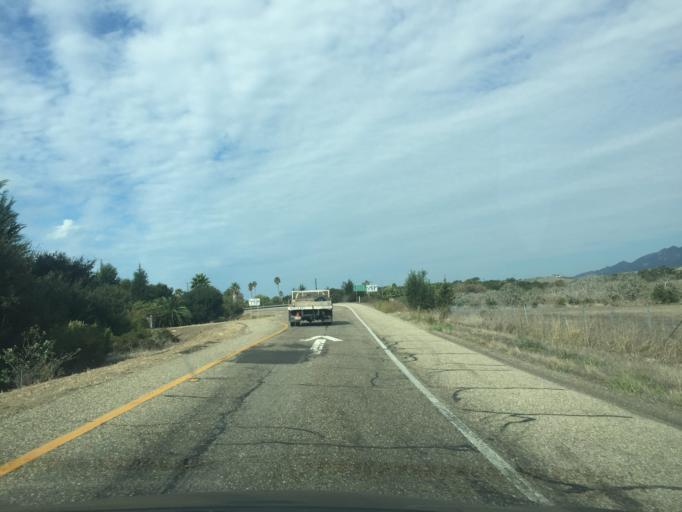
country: US
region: California
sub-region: Santa Barbara County
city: Isla Vista
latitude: 34.4355
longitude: -119.8681
